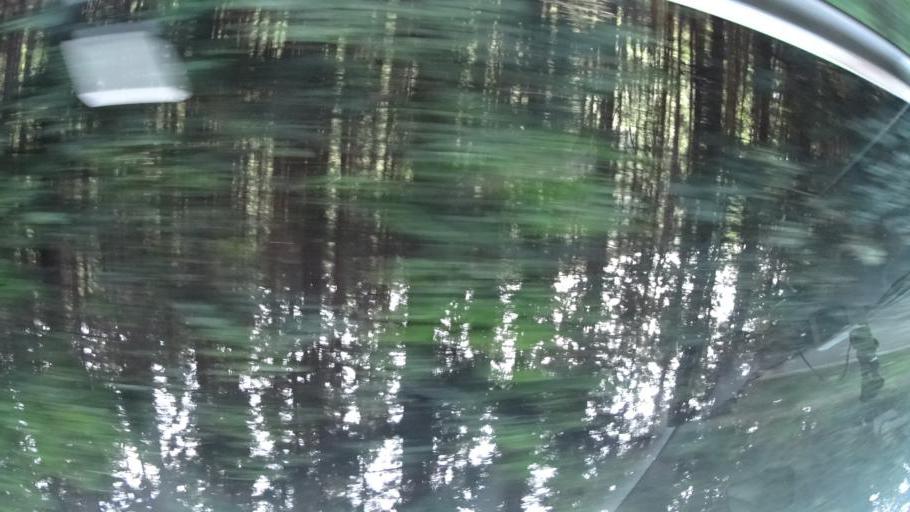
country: DE
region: Baden-Wuerttemberg
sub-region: Karlsruhe Region
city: Heddesbach
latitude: 49.4972
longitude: 8.8466
